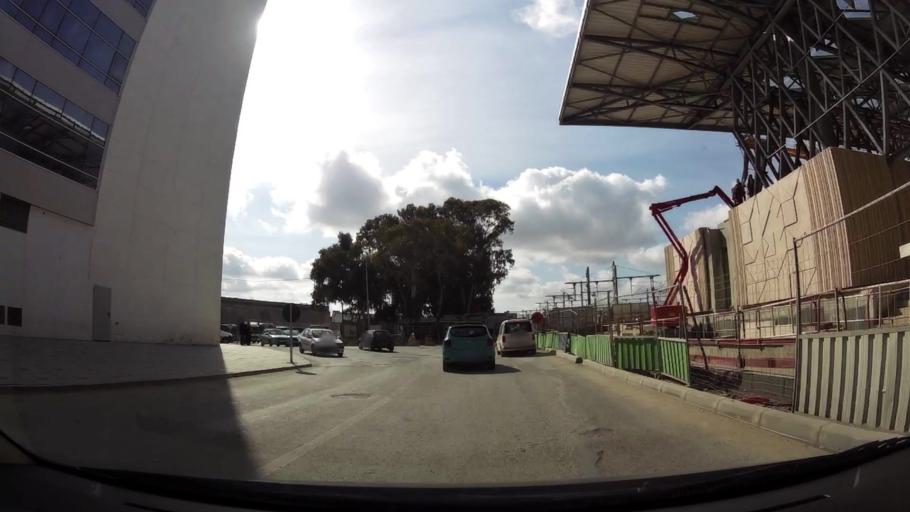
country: MA
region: Tanger-Tetouan
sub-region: Tanger-Assilah
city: Tangier
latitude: 35.7710
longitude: -5.7853
